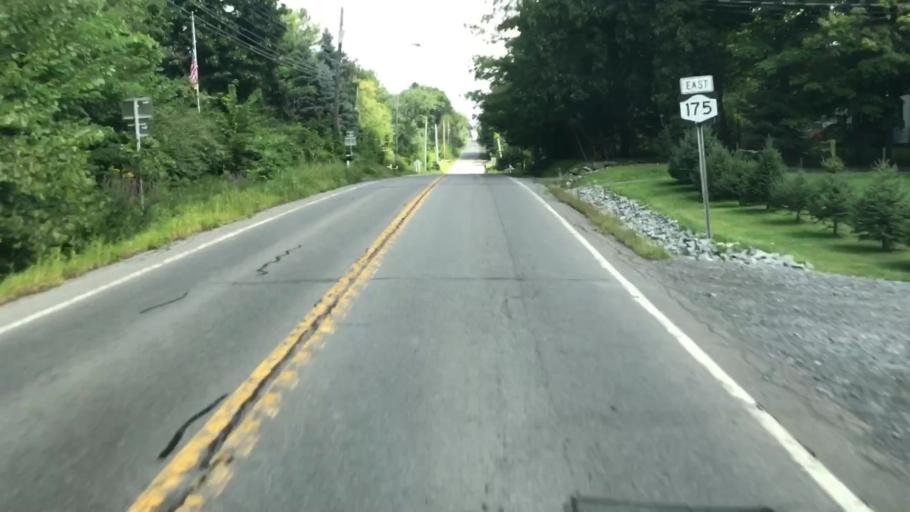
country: US
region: New York
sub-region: Onondaga County
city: Marcellus
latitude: 42.9829
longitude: -76.3291
